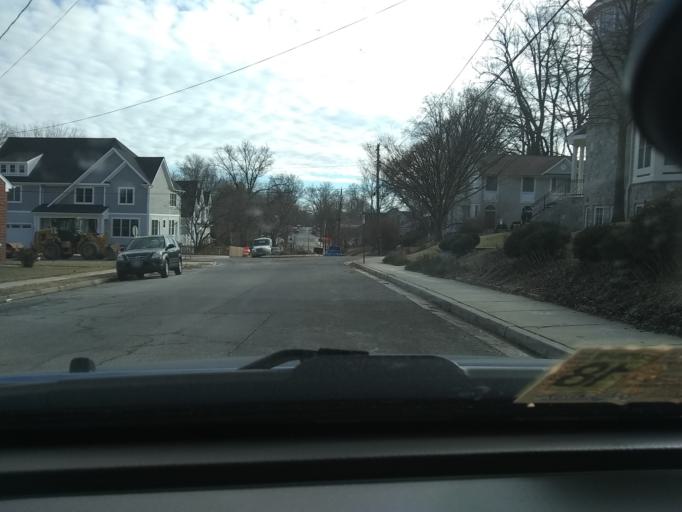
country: US
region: Virginia
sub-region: Fairfax County
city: Seven Corners
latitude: 38.8945
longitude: -77.1417
